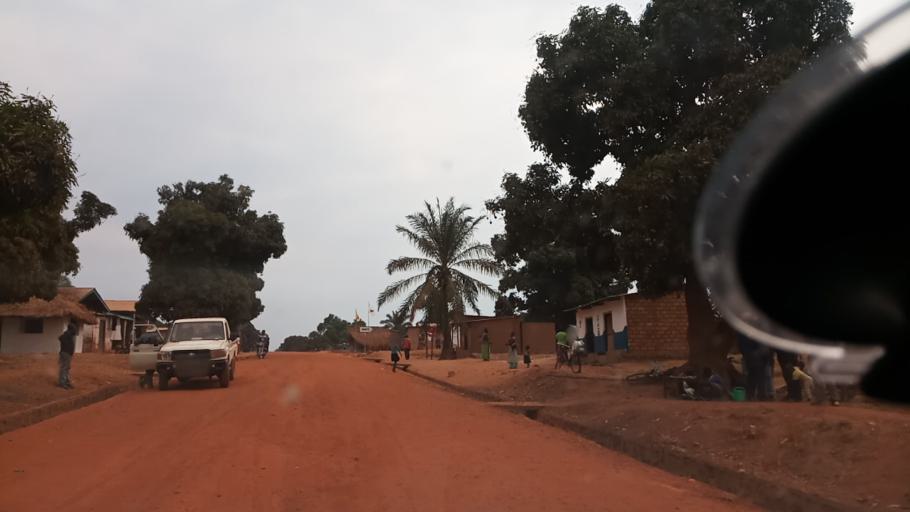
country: ZM
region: Luapula
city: Nchelenge
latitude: -9.1006
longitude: 28.3007
